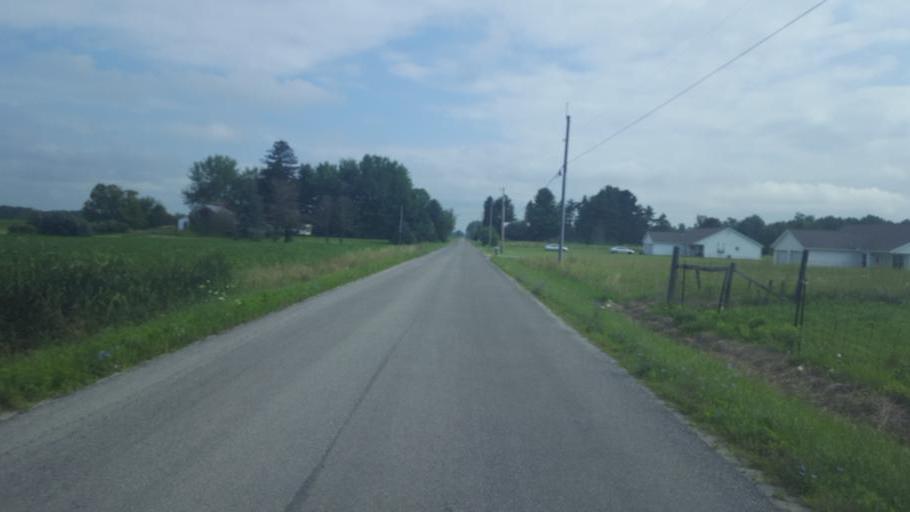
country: US
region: Ohio
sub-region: Crawford County
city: Galion
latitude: 40.6716
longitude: -82.7843
